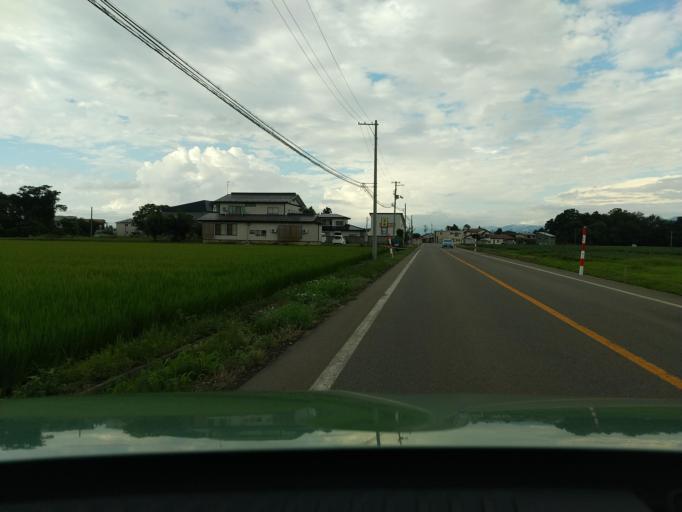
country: JP
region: Akita
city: Yokotemachi
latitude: 39.3306
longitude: 140.4864
